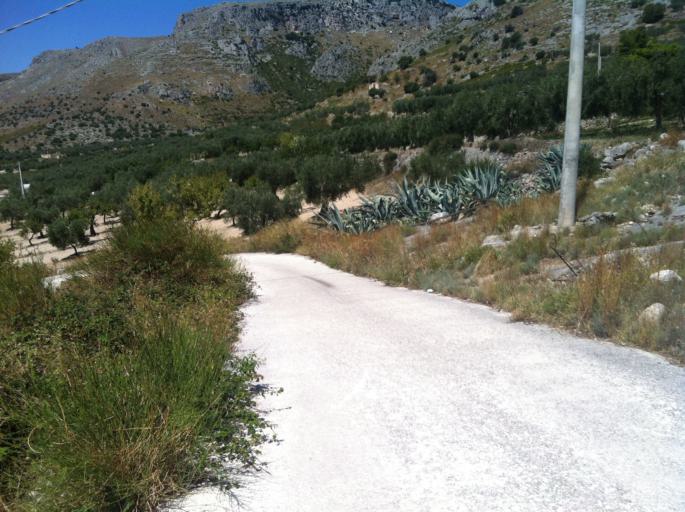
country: IT
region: Apulia
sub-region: Provincia di Foggia
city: Manfredonia
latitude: 41.6630
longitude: 15.9180
